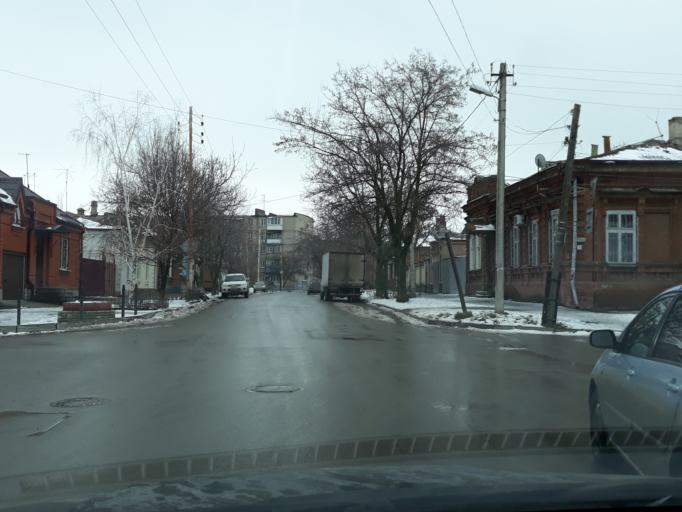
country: RU
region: Rostov
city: Taganrog
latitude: 47.2146
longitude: 38.9242
